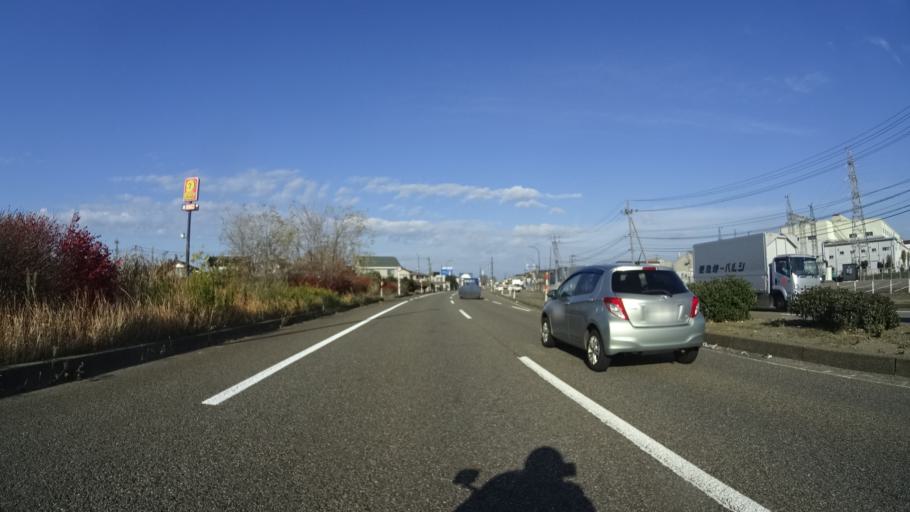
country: JP
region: Niigata
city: Joetsu
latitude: 37.1756
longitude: 138.2666
